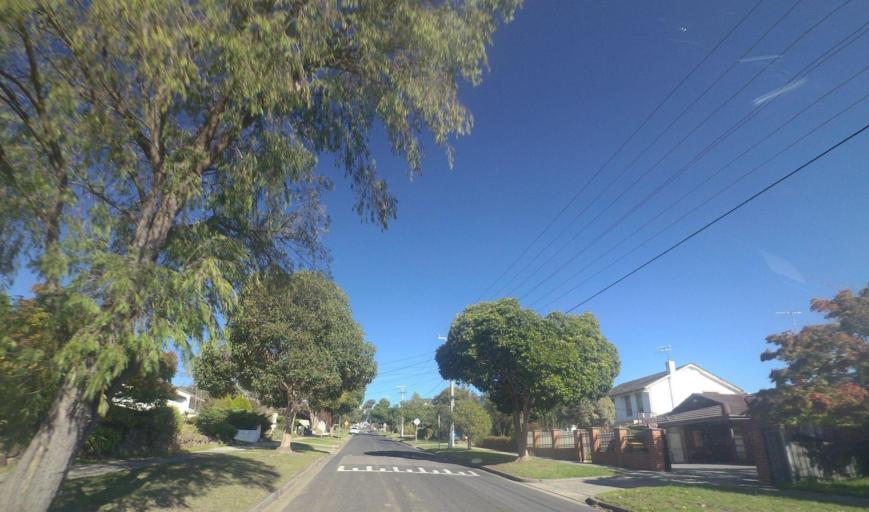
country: AU
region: Victoria
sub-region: Manningham
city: Doncaster
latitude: -37.7833
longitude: 145.1301
